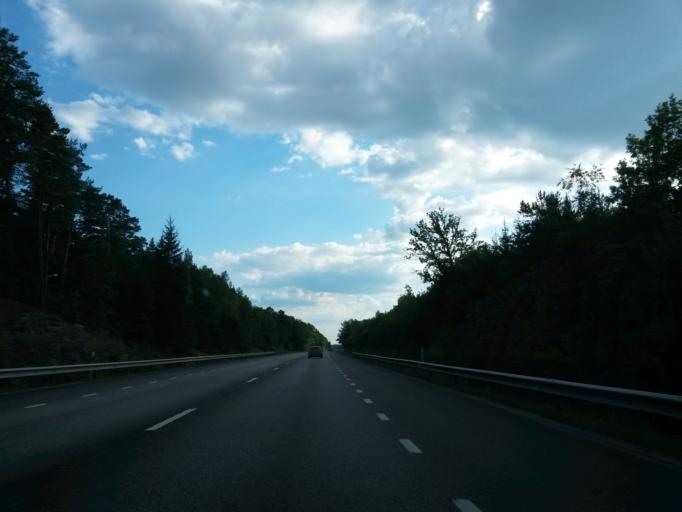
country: SE
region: Vaestra Goetaland
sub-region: Vargarda Kommun
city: Vargarda
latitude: 58.1250
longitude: 12.8532
